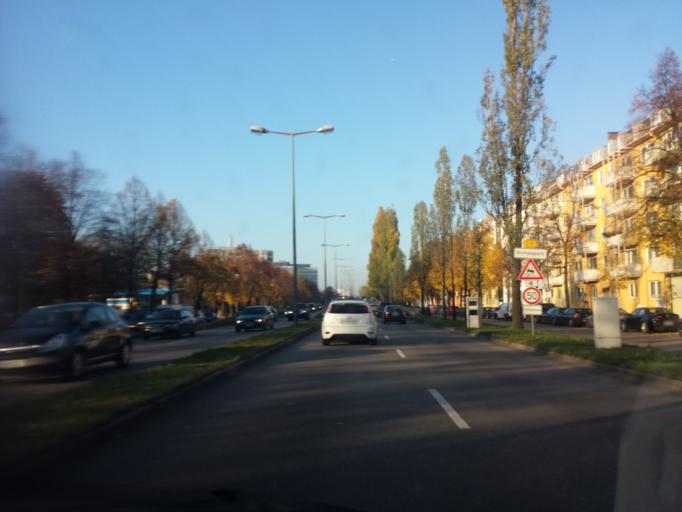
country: DE
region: Bavaria
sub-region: Upper Bavaria
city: Munich
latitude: 48.1623
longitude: 11.5377
